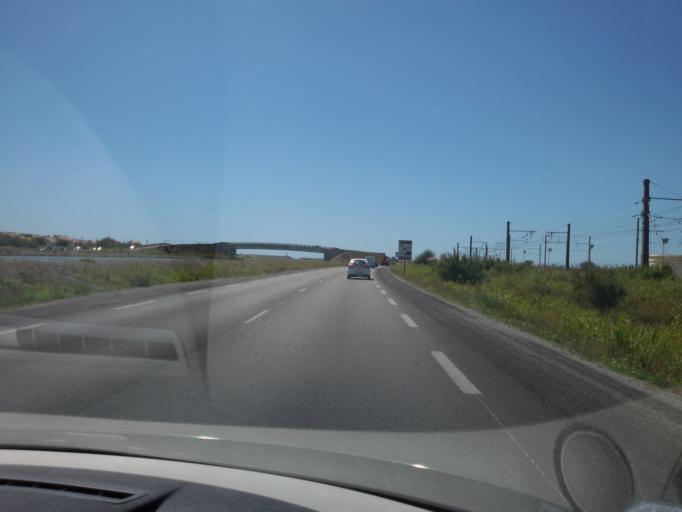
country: FR
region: Languedoc-Roussillon
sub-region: Departement de l'Herault
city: Frontignan
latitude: 43.4311
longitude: 3.7551
